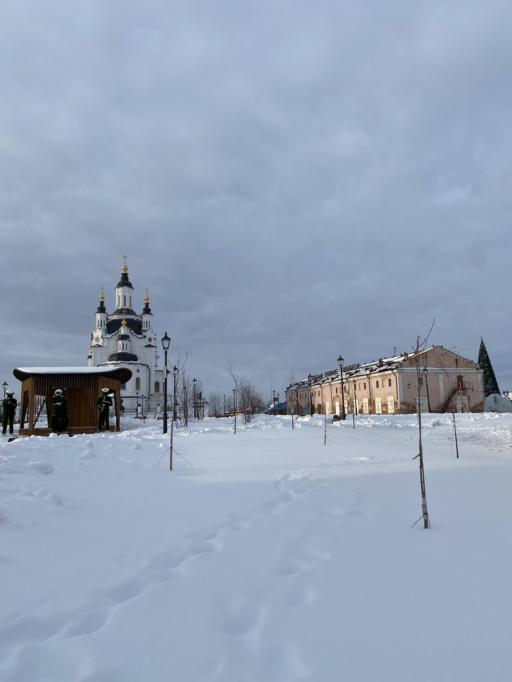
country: RU
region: Tjumen
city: Tobol'sk
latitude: 58.1959
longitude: 68.2458
